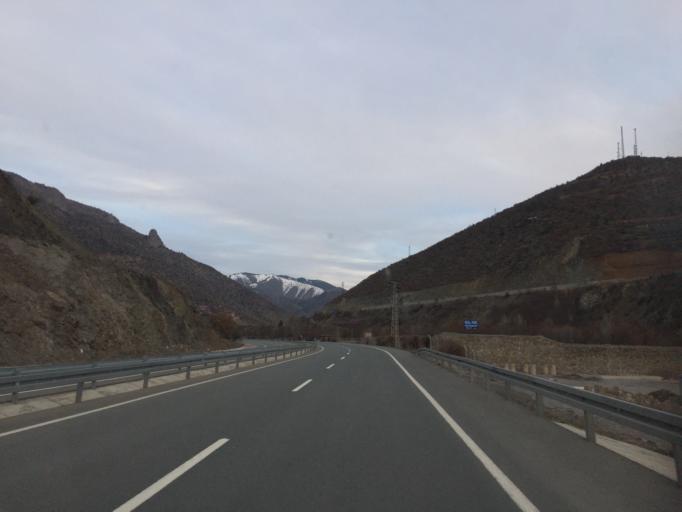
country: TR
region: Gumushane
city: Torul
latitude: 40.5228
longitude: 39.3544
